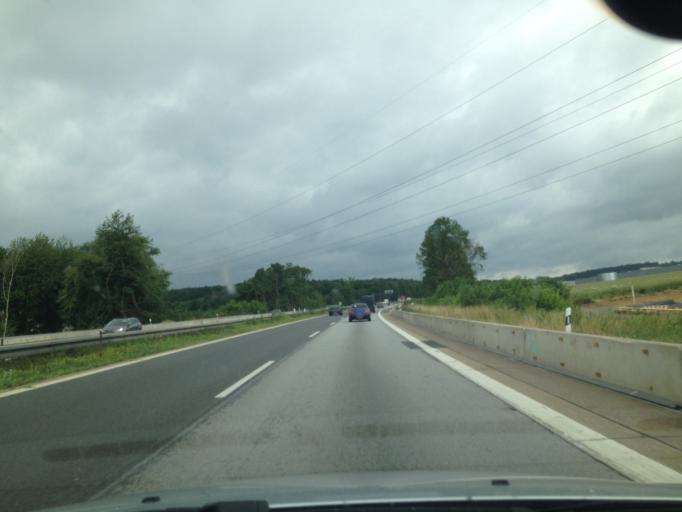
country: DE
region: Bavaria
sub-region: Regierungsbezirk Unterfranken
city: Esselbach
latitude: 49.8205
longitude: 9.5487
